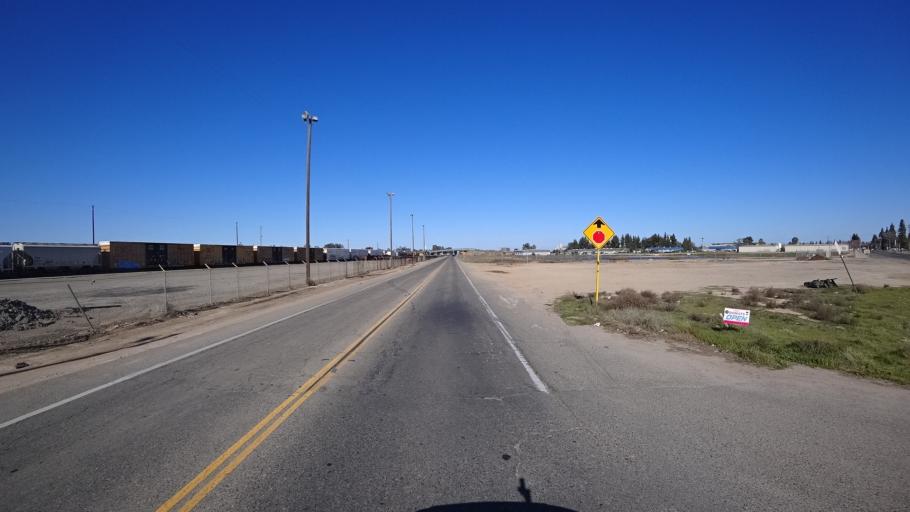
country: US
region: California
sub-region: Fresno County
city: West Park
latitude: 36.7896
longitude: -119.8536
